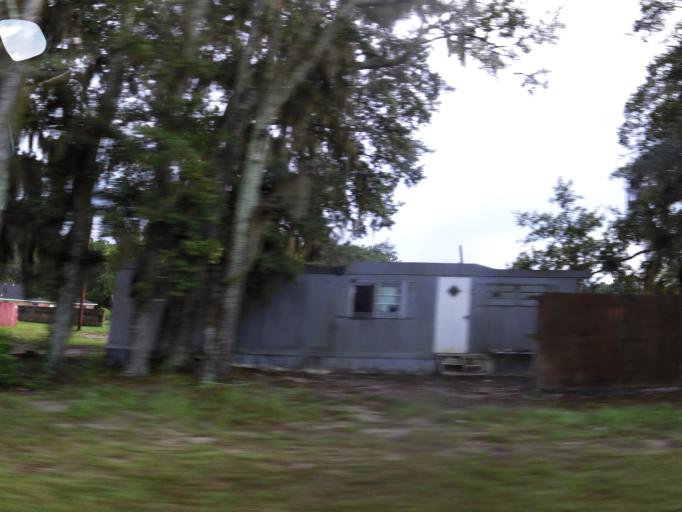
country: US
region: Georgia
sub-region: Liberty County
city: Walthourville
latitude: 31.7819
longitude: -81.6174
